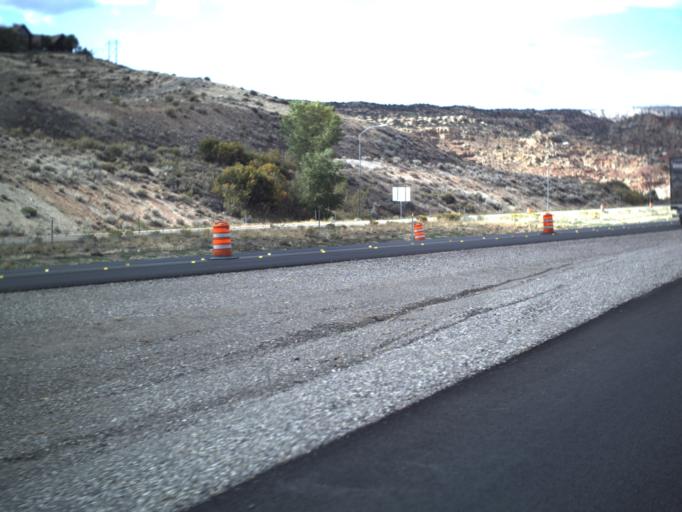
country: US
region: Utah
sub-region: Sevier County
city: Richfield
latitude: 38.7535
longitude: -112.1047
